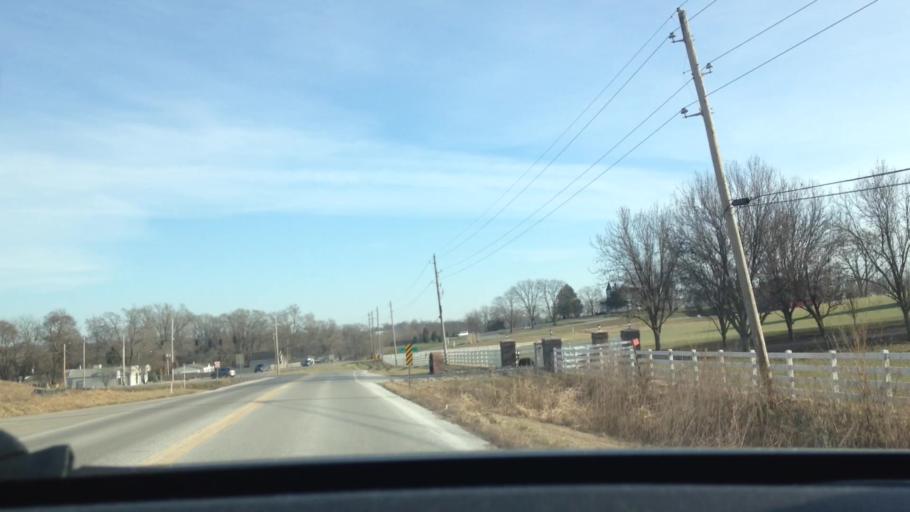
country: US
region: Missouri
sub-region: Platte County
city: Platte City
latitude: 39.3786
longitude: -94.7982
